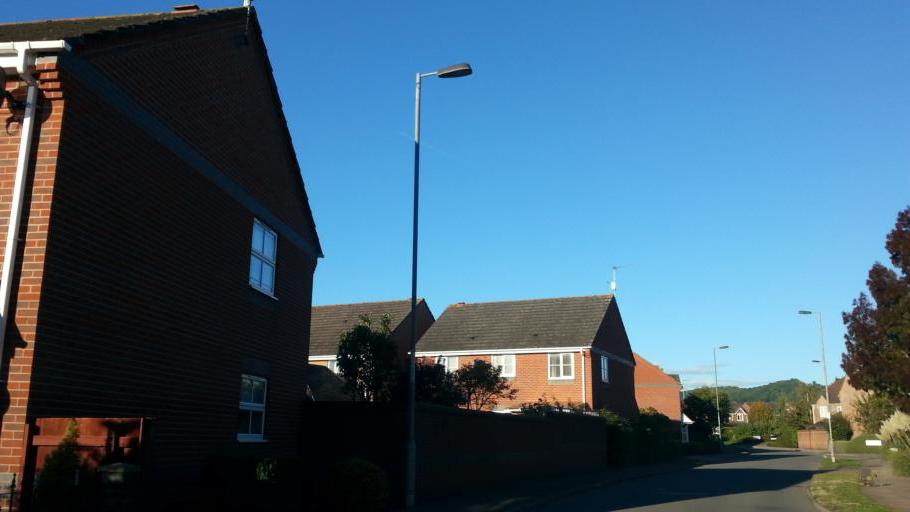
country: GB
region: Wales
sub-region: Monmouthshire
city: Monmouth
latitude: 51.8159
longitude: -2.7310
